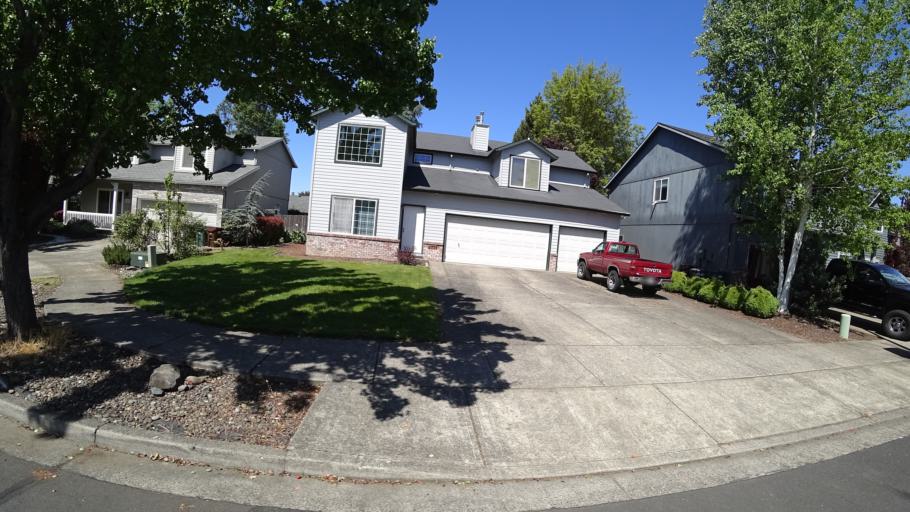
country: US
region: Oregon
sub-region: Washington County
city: Hillsboro
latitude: 45.5081
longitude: -122.9546
